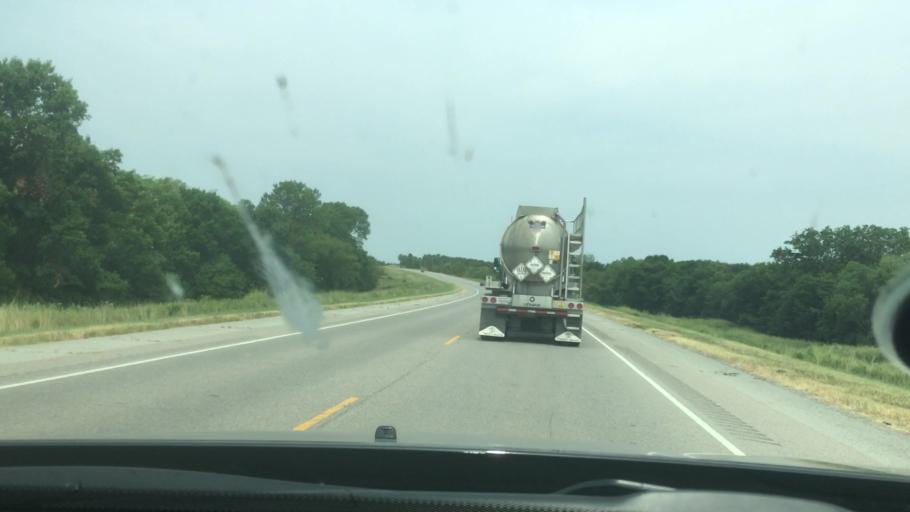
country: US
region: Oklahoma
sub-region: Pontotoc County
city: Ada
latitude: 34.6400
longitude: -96.4850
